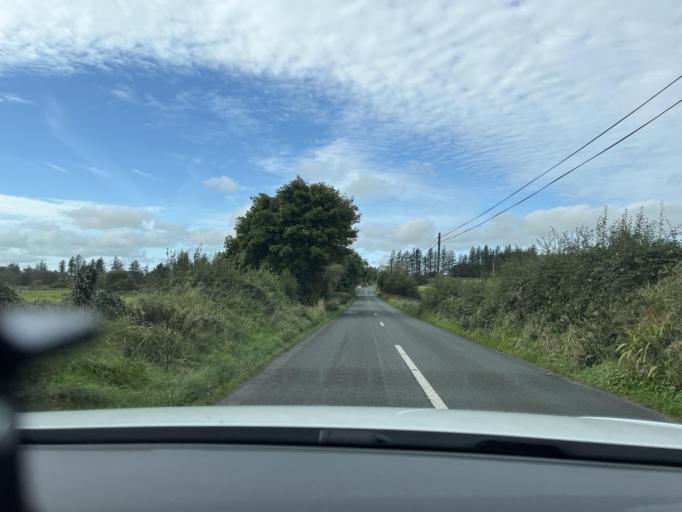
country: IE
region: Connaught
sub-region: Sligo
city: Ballymote
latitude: 54.0292
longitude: -8.4101
